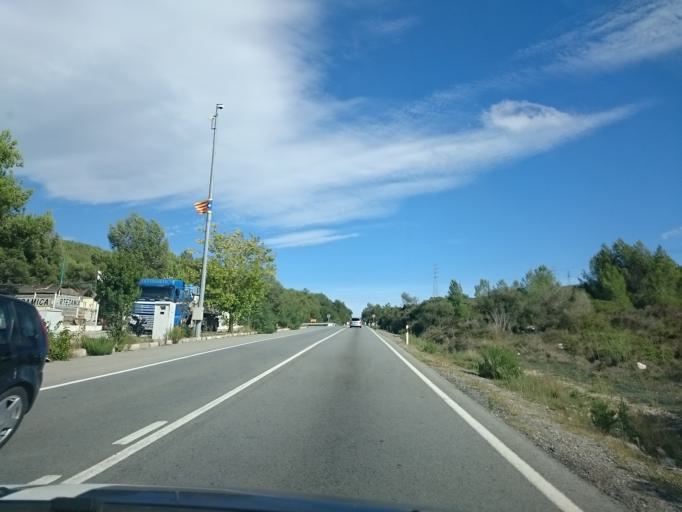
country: ES
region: Catalonia
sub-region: Provincia de Barcelona
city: Subirats
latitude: 41.3943
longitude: 1.8561
